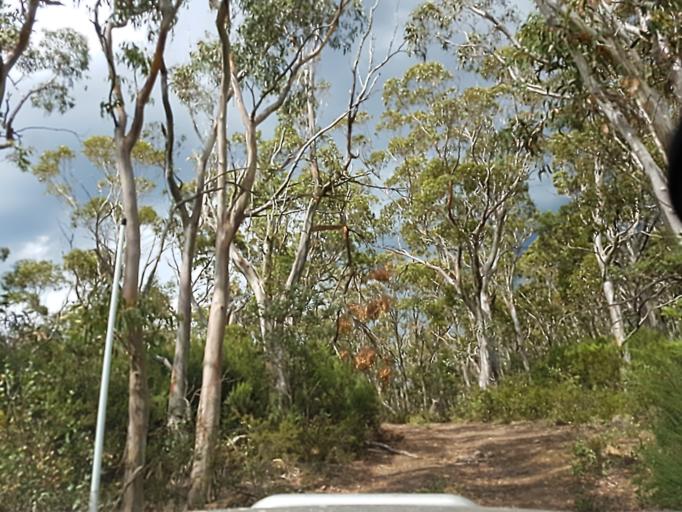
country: AU
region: New South Wales
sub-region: Snowy River
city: Jindabyne
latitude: -36.8792
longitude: 148.1899
